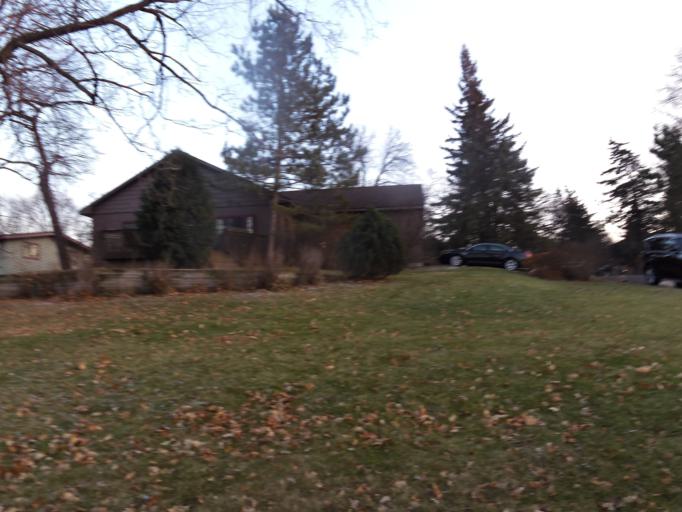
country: US
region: Minnesota
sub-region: Scott County
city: Prior Lake
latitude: 44.7101
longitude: -93.4423
